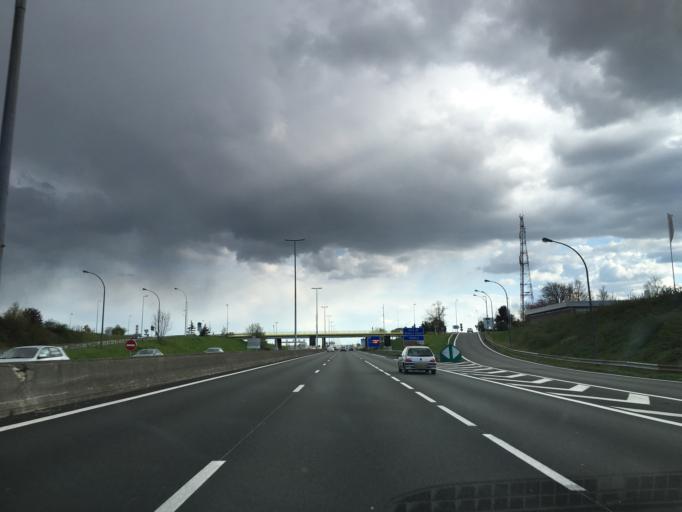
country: FR
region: Ile-de-France
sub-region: Departement du Val-d'Oise
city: Survilliers
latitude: 49.0886
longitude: 2.5507
